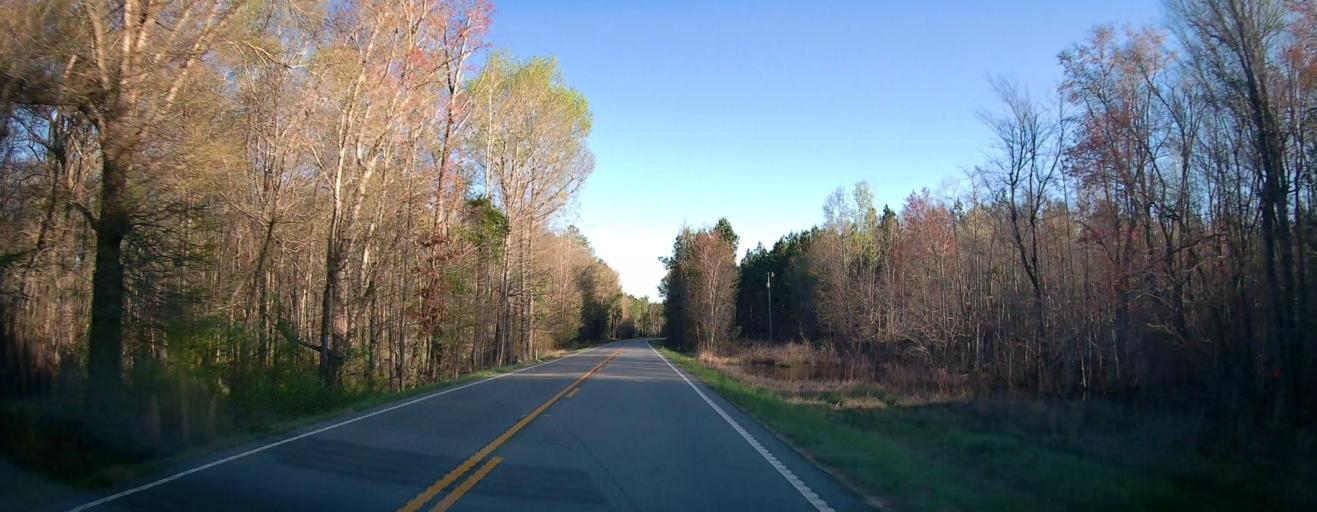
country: US
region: Georgia
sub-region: Pulaski County
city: Hawkinsville
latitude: 32.1992
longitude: -83.3731
